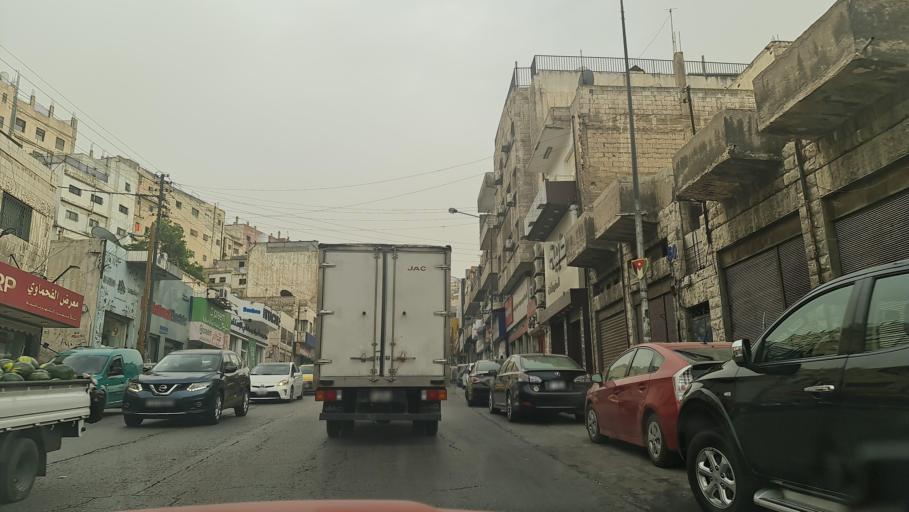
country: JO
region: Amman
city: Amman
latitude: 31.9414
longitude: 35.9292
